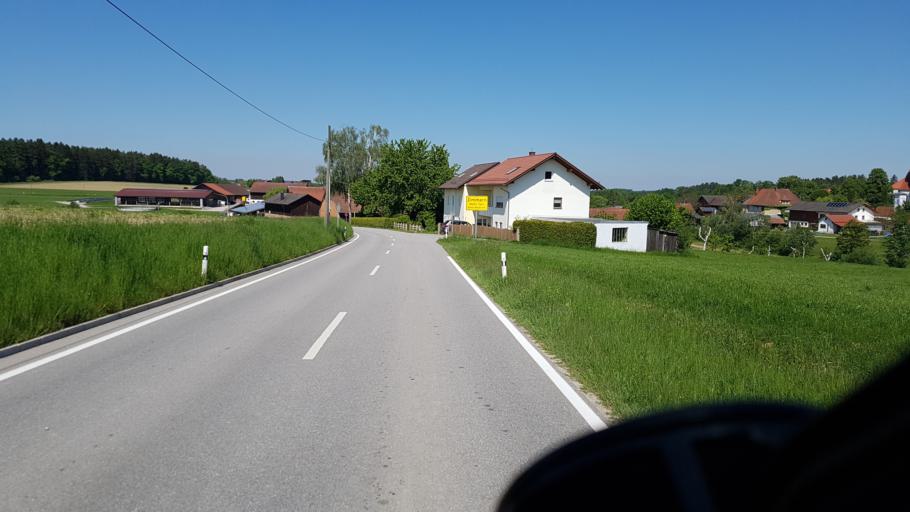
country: DE
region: Bavaria
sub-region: Lower Bavaria
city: Reut
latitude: 48.3405
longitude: 12.9238
